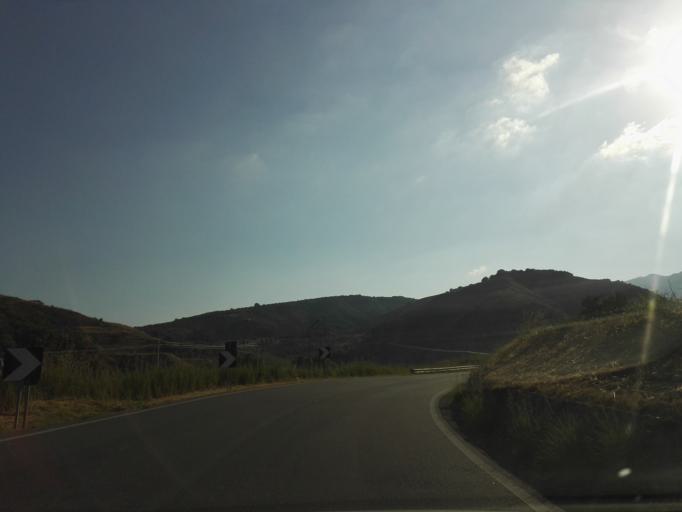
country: IT
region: Calabria
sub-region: Provincia di Reggio Calabria
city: Stilo
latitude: 38.4645
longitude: 16.5017
